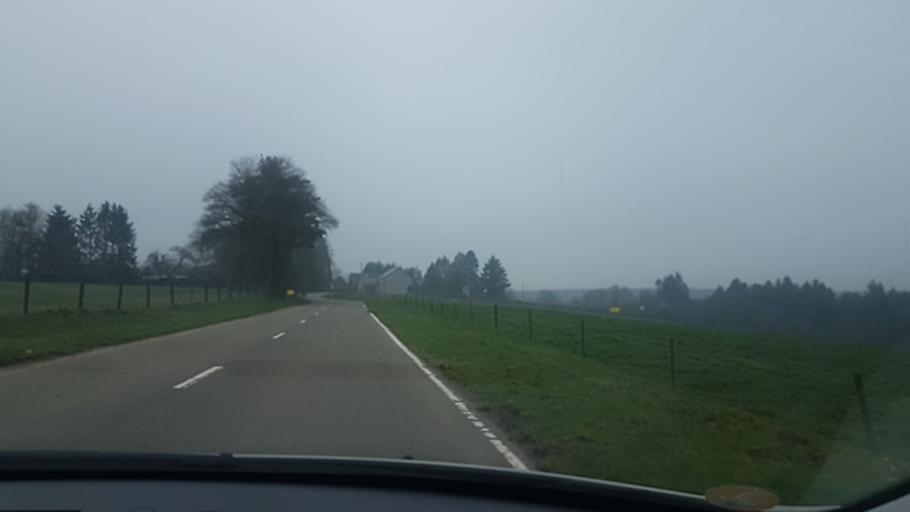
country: FR
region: Champagne-Ardenne
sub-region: Departement des Ardennes
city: Haybes
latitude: 50.0352
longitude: 4.6726
